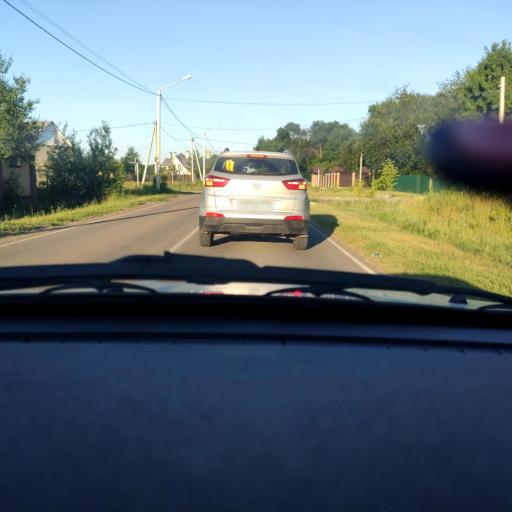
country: RU
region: Voronezj
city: Ramon'
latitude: 51.8904
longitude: 39.2640
